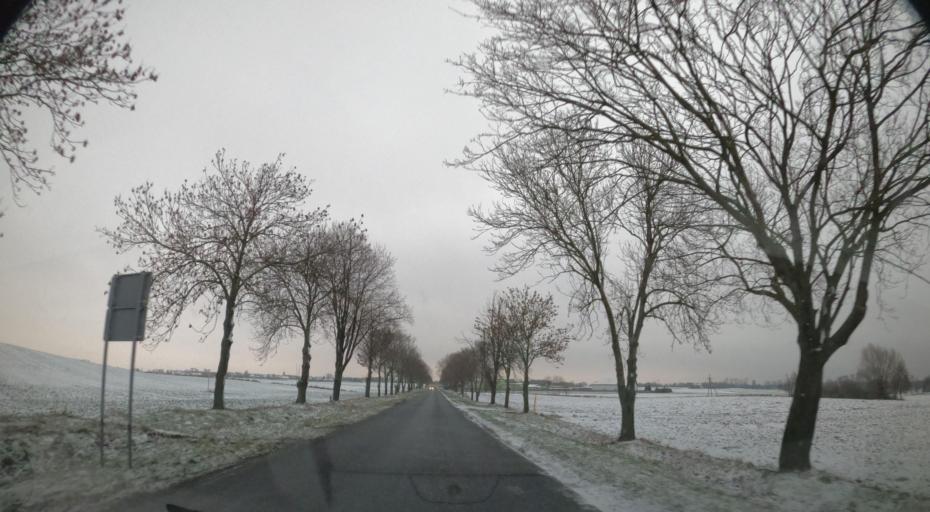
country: PL
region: Kujawsko-Pomorskie
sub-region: Powiat lipnowski
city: Wielgie
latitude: 52.7319
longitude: 19.2797
